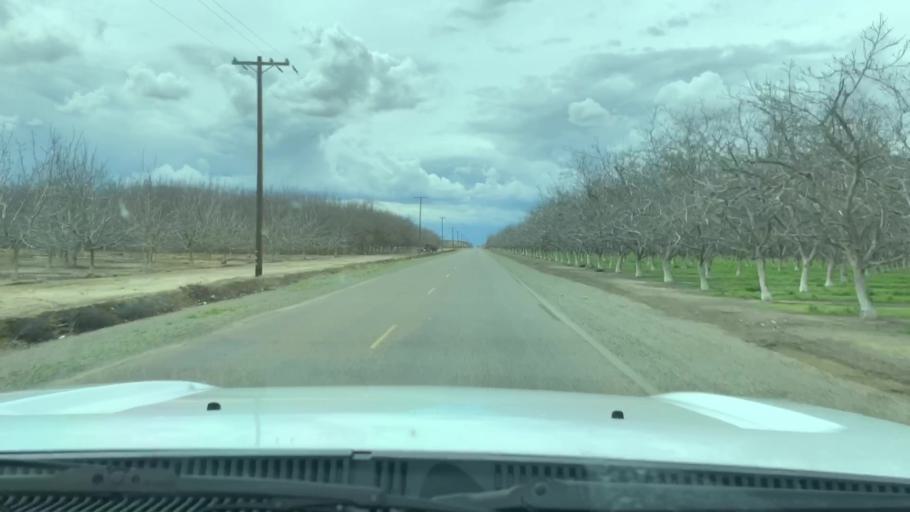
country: US
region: California
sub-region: Fresno County
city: Laton
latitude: 36.4894
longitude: -119.7572
